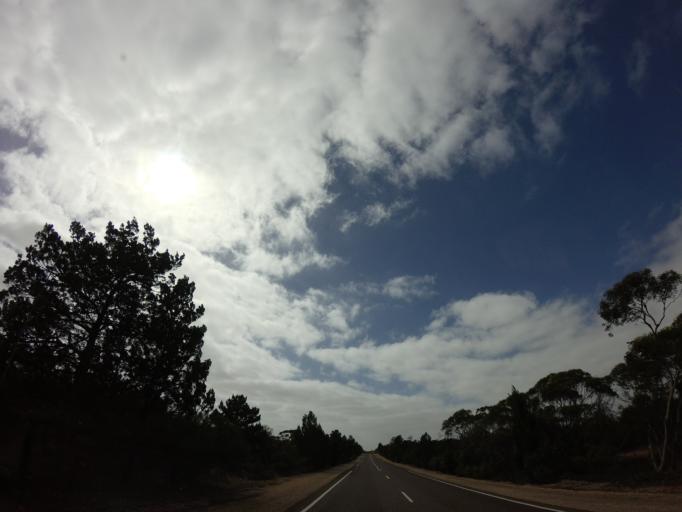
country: AU
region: South Australia
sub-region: Streaky Bay
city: Streaky Bay
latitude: -32.7130
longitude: 134.8249
